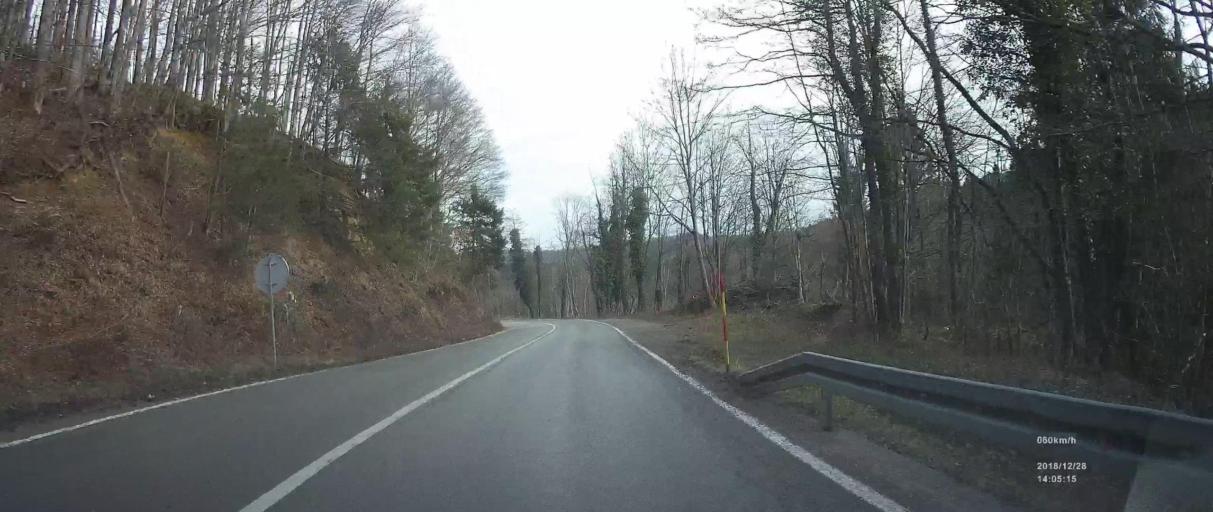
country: SI
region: Kostel
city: Kostel
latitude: 45.4401
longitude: 14.9255
